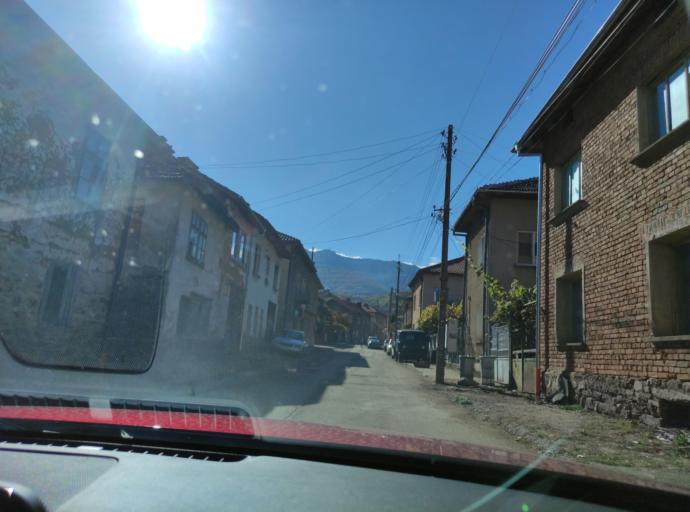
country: BG
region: Montana
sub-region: Obshtina Chiprovtsi
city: Chiprovtsi
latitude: 43.3817
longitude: 22.8794
